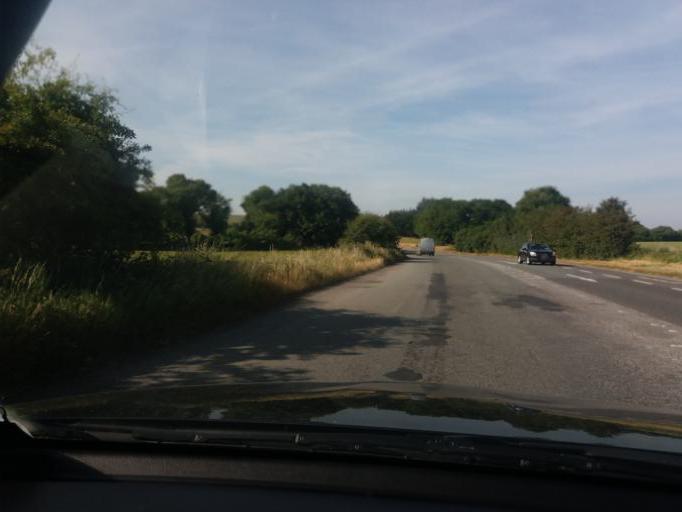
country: IE
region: Leinster
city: Lusk
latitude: 53.5259
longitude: -6.1889
